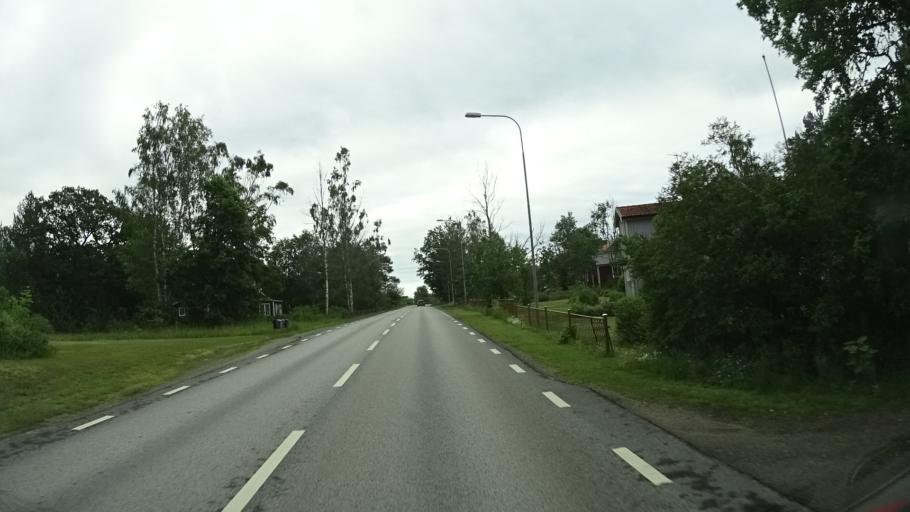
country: SE
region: Kalmar
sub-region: Oskarshamns Kommun
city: Oskarshamn
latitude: 57.3161
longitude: 16.2759
